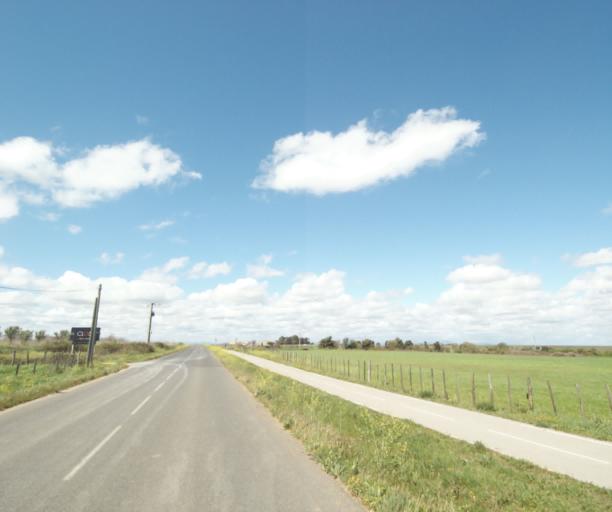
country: FR
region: Languedoc-Roussillon
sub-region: Departement de l'Herault
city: Perols
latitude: 43.5587
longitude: 3.9295
